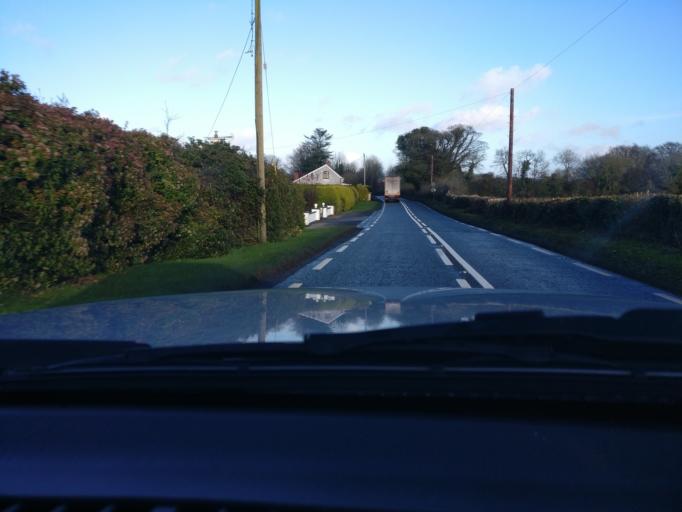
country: IE
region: Leinster
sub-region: An Mhi
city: Athboy
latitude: 53.6454
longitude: -7.0352
